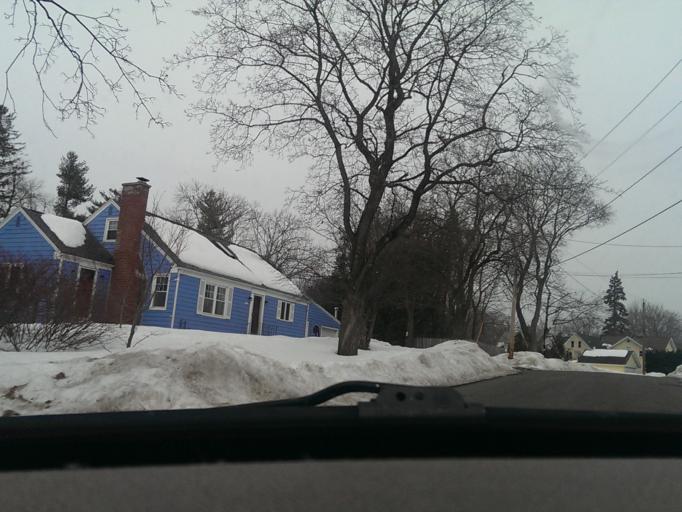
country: US
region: Massachusetts
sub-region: Hampden County
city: East Longmeadow
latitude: 42.0707
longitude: -72.5168
